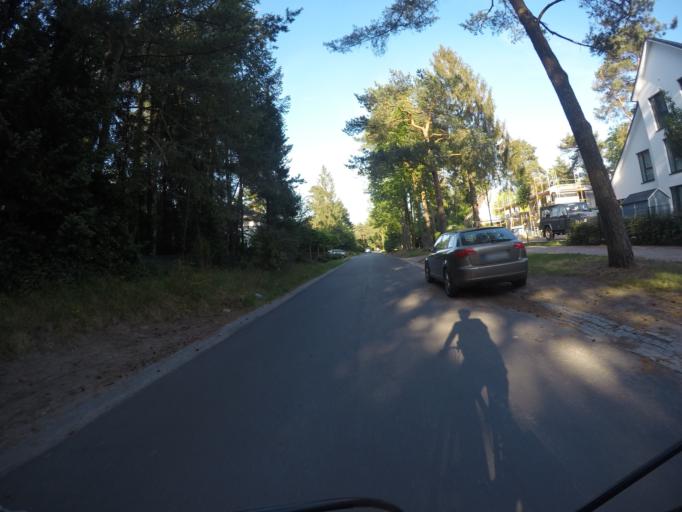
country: DE
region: Schleswig-Holstein
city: Wedel
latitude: 53.5864
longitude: 9.7400
